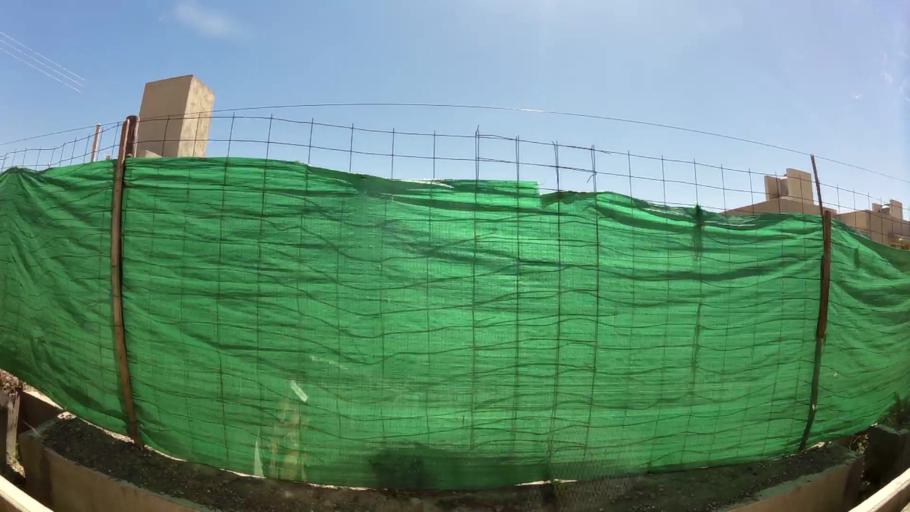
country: AR
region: Mendoza
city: Las Heras
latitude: -32.8382
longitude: -68.8636
